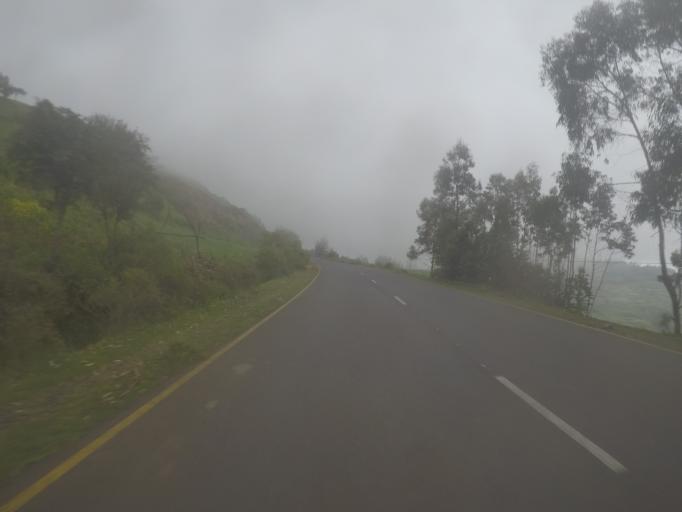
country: ET
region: Amhara
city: Gondar
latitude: 12.7431
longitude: 37.5214
